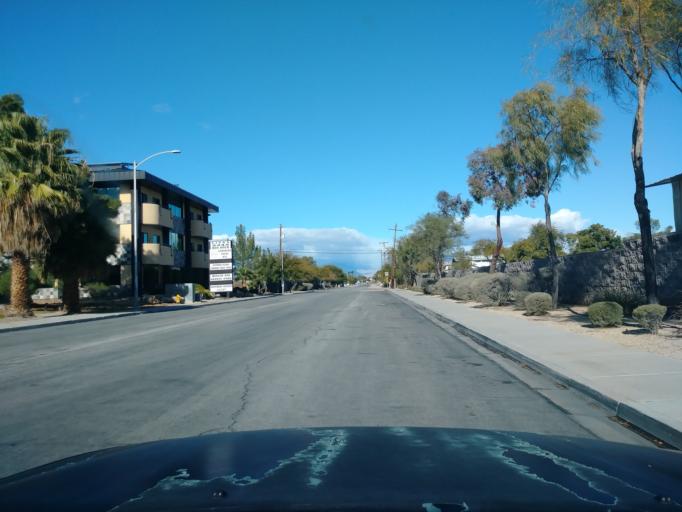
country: US
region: Nevada
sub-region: Clark County
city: Spring Valley
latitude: 36.1453
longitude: -115.2231
